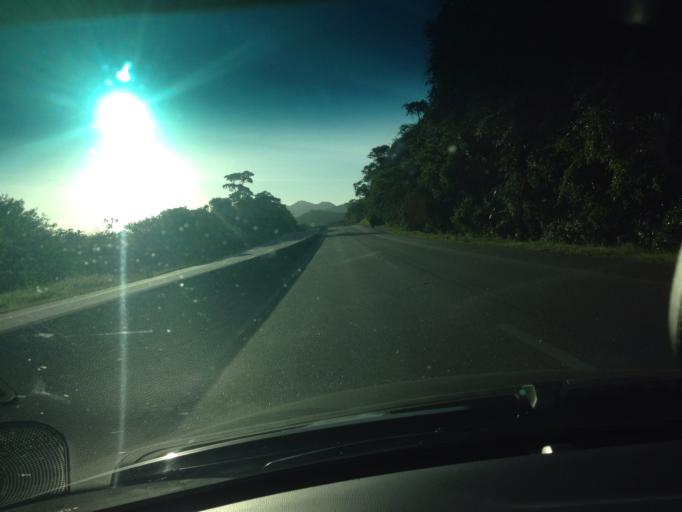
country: BR
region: Espirito Santo
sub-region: Guarapari
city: Guarapari
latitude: -20.6114
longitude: -40.4787
